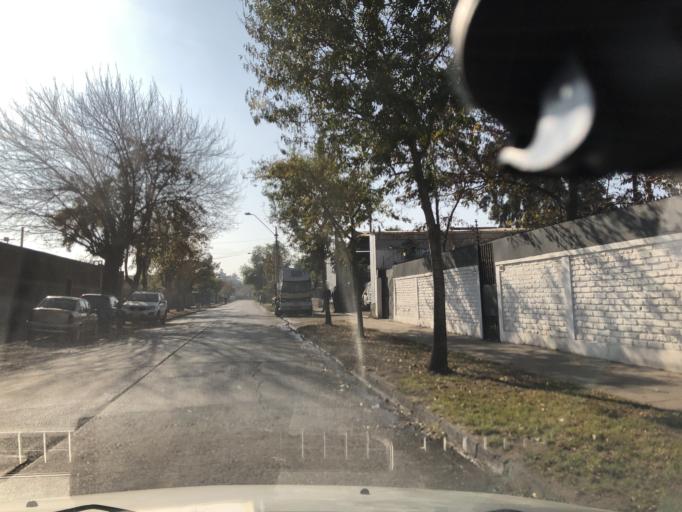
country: CL
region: Santiago Metropolitan
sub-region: Provincia de Cordillera
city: Puente Alto
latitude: -33.6279
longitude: -70.5845
